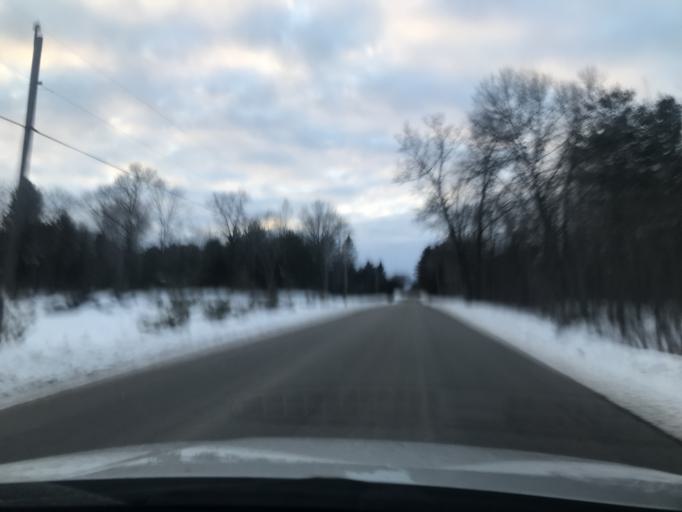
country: US
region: Wisconsin
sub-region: Marinette County
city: Peshtigo
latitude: 45.1644
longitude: -87.7325
